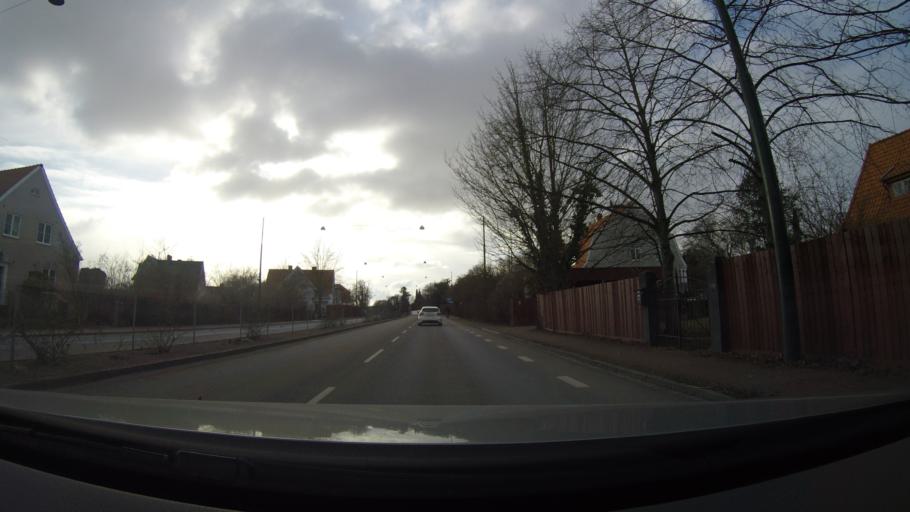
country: SE
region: Skane
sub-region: Malmo
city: Malmoe
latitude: 55.5876
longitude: 12.9546
